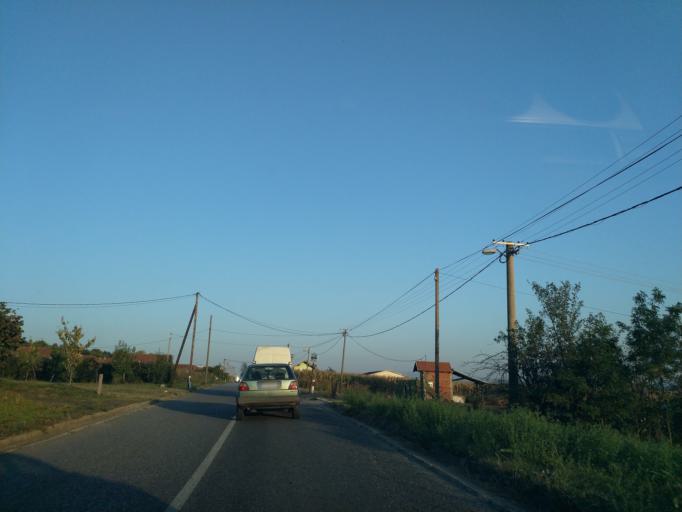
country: RS
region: Central Serbia
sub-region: Rasinski Okrug
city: Trstenik
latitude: 43.6313
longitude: 21.0376
